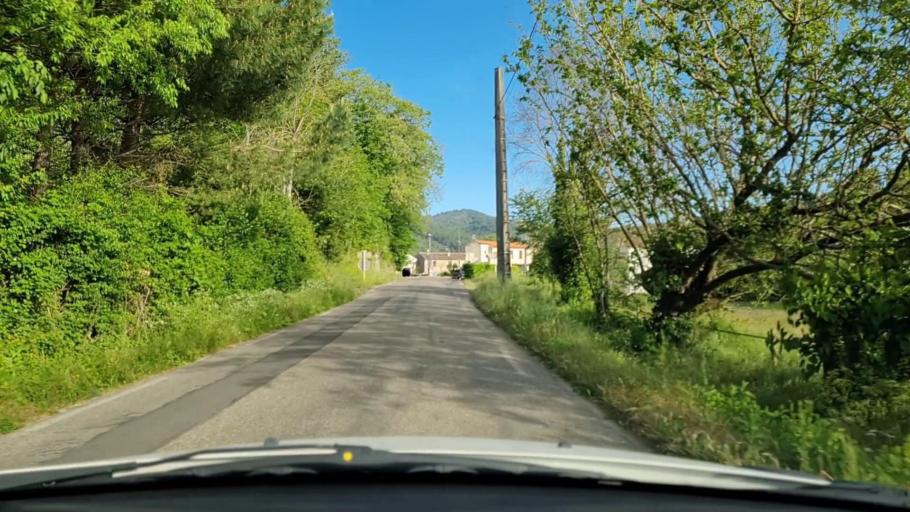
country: FR
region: Languedoc-Roussillon
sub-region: Departement du Gard
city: Cendras
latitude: 44.1537
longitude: 4.0395
